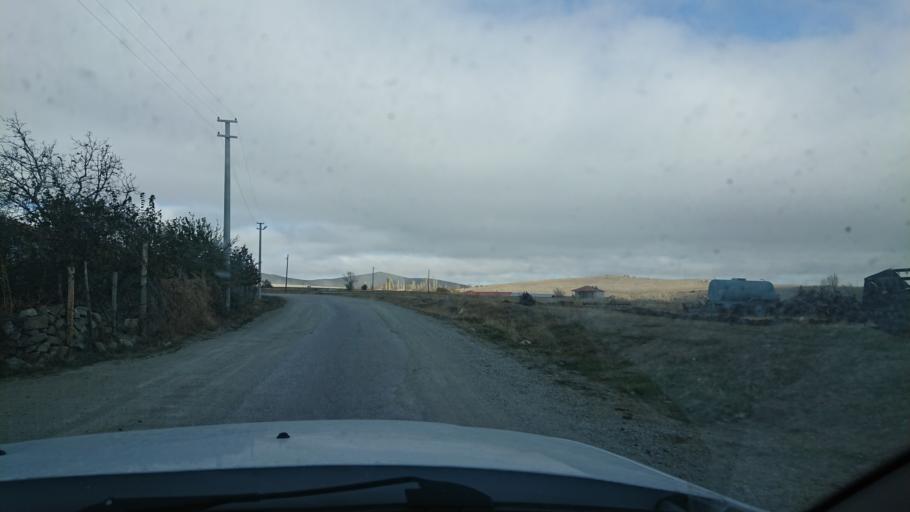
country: TR
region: Aksaray
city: Ortakoy
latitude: 38.7610
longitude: 34.0123
